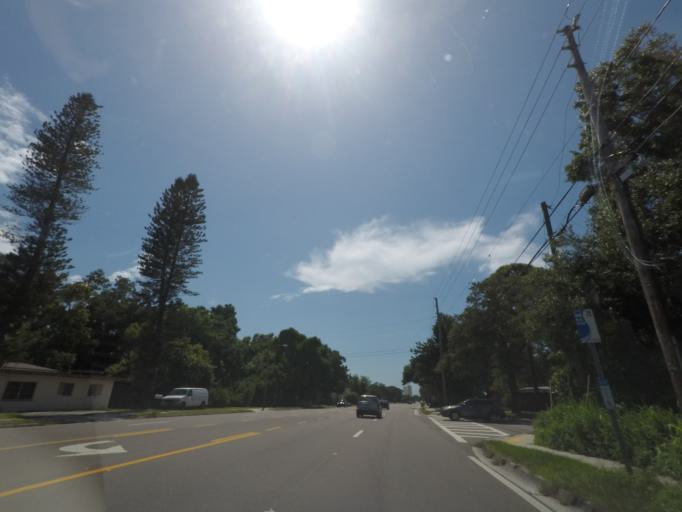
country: US
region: Florida
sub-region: Pinellas County
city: South Pasadena
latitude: 27.7579
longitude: -82.7264
